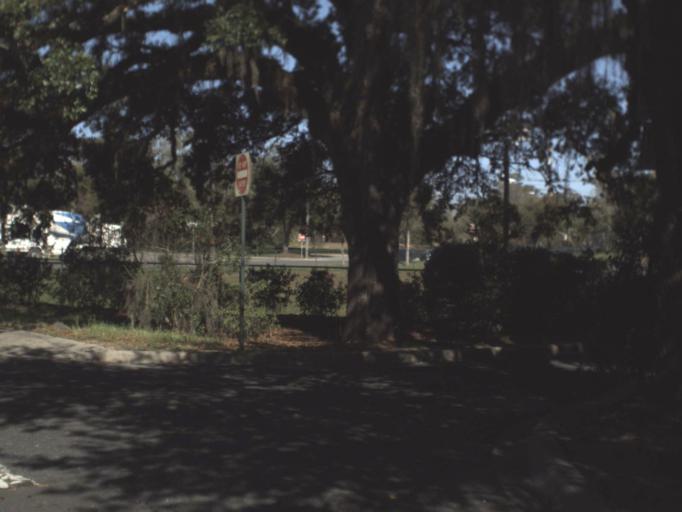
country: US
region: Florida
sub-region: Leon County
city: Tallahassee
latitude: 30.3983
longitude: -84.2795
